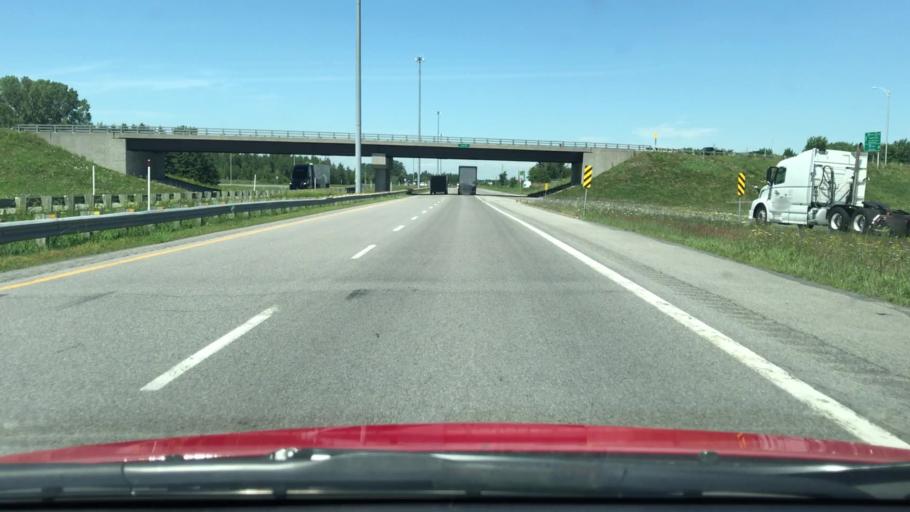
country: CA
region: Quebec
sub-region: Monteregie
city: Napierville
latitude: 45.1924
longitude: -73.4529
